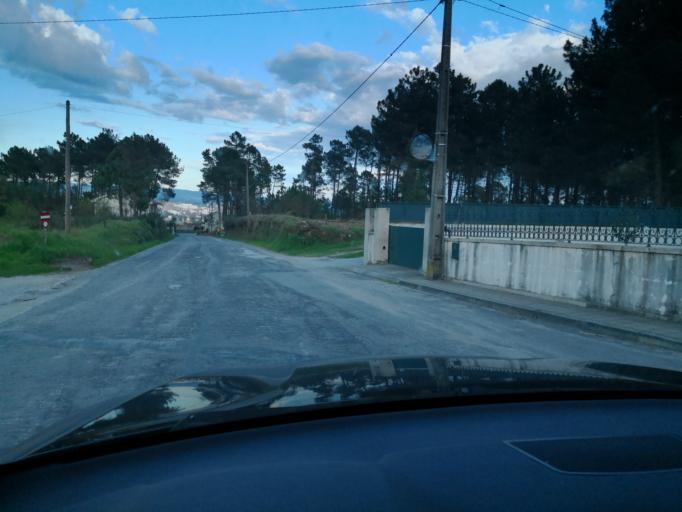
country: PT
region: Vila Real
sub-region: Vila Real
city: Vila Real
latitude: 41.3001
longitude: -7.7758
